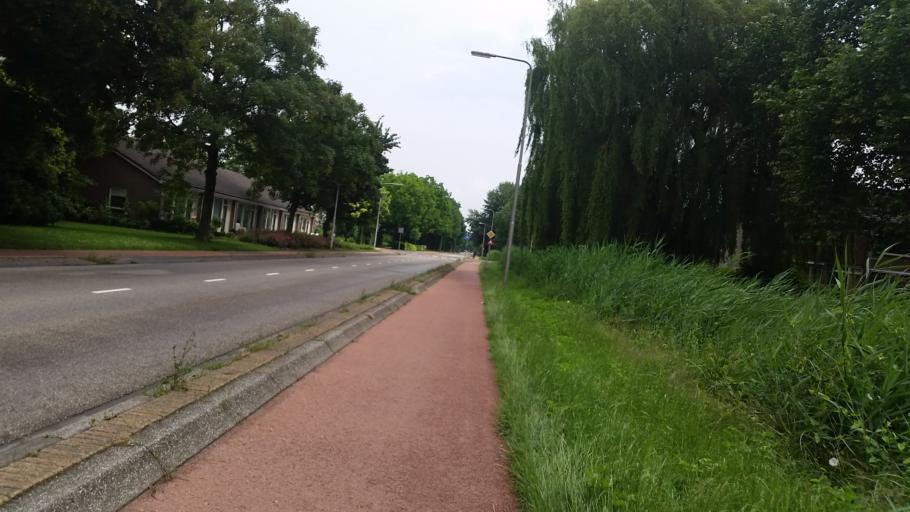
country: NL
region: Gelderland
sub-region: Gemeente Geldermalsen
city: Geldermalsen
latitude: 51.8769
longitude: 5.2950
